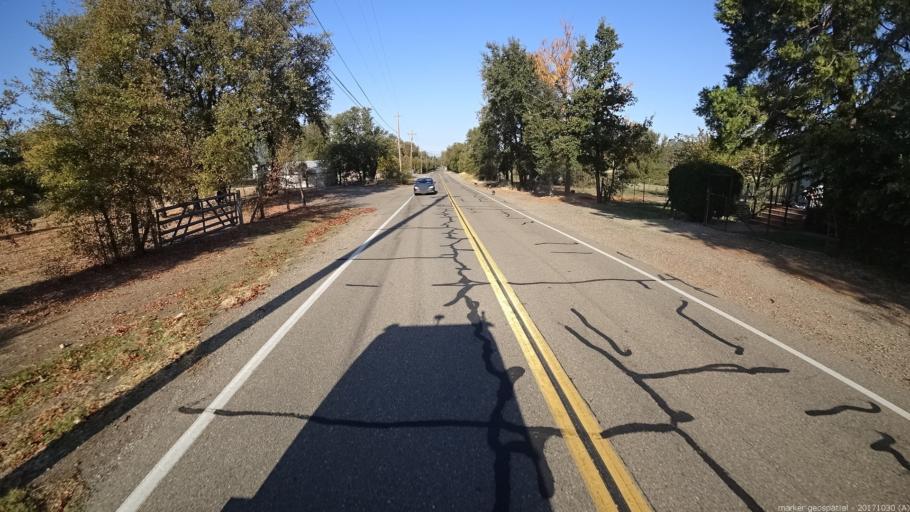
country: US
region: California
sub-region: Shasta County
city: Palo Cedro
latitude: 40.5498
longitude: -122.1795
